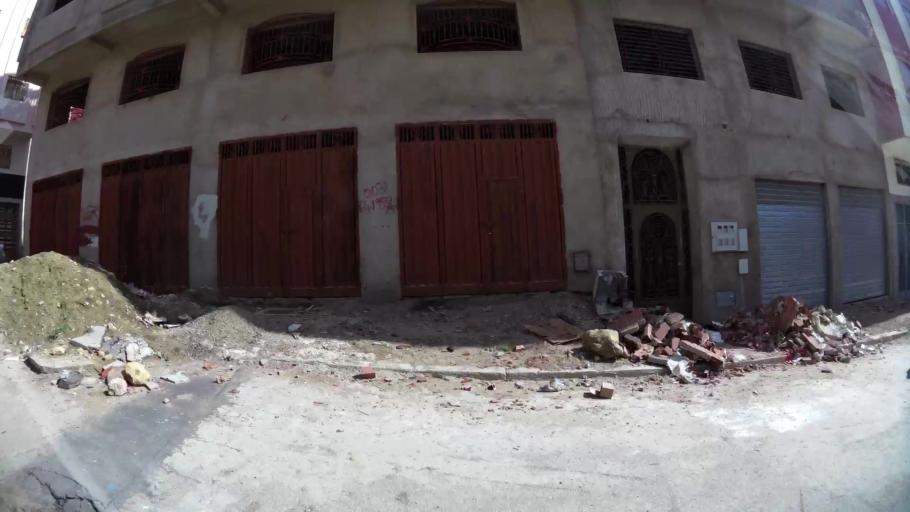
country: MA
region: Tanger-Tetouan
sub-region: Tanger-Assilah
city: Tangier
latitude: 35.7249
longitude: -5.8138
